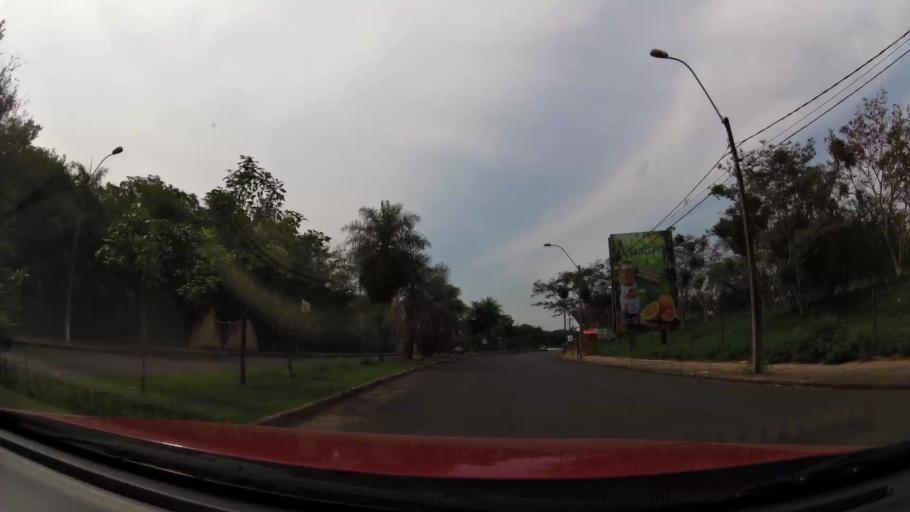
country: PY
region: Asuncion
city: Asuncion
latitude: -25.2789
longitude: -57.5790
